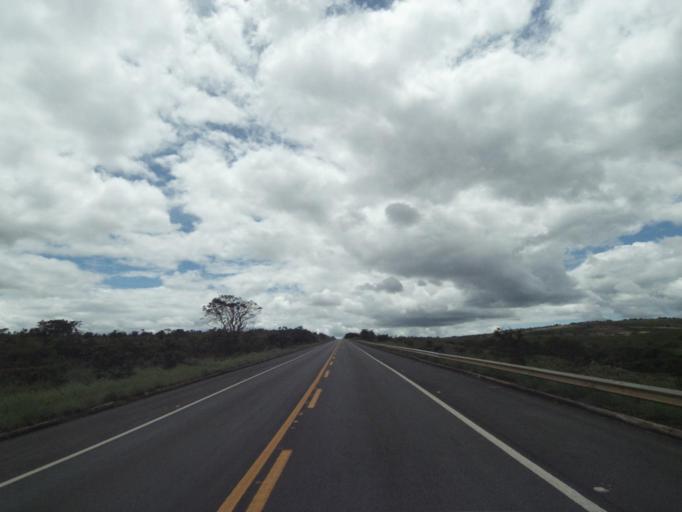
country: BR
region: Federal District
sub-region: Brasilia
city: Brasilia
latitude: -15.7443
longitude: -48.3577
